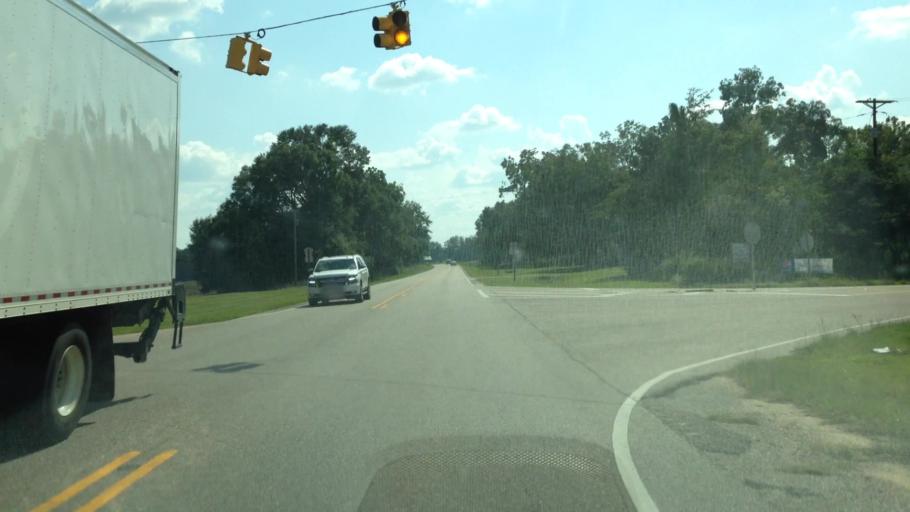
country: US
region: Florida
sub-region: Okaloosa County
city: Crestview
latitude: 31.0222
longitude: -86.6128
